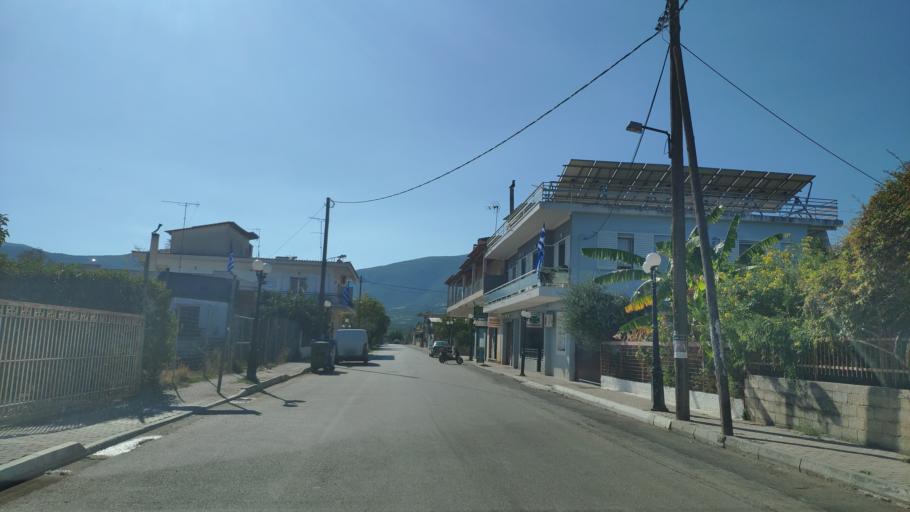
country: GR
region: Peloponnese
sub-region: Nomos Korinthias
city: Khiliomodhi
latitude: 37.8078
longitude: 22.8699
